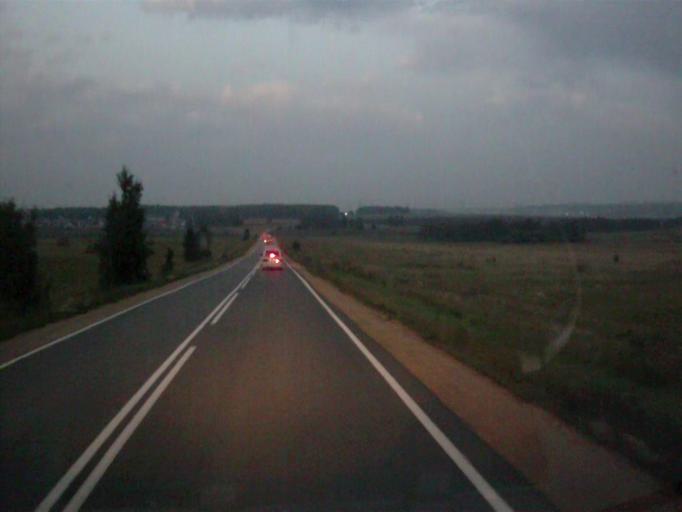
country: RU
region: Chelyabinsk
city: Argayash
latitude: 55.2090
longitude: 60.8499
